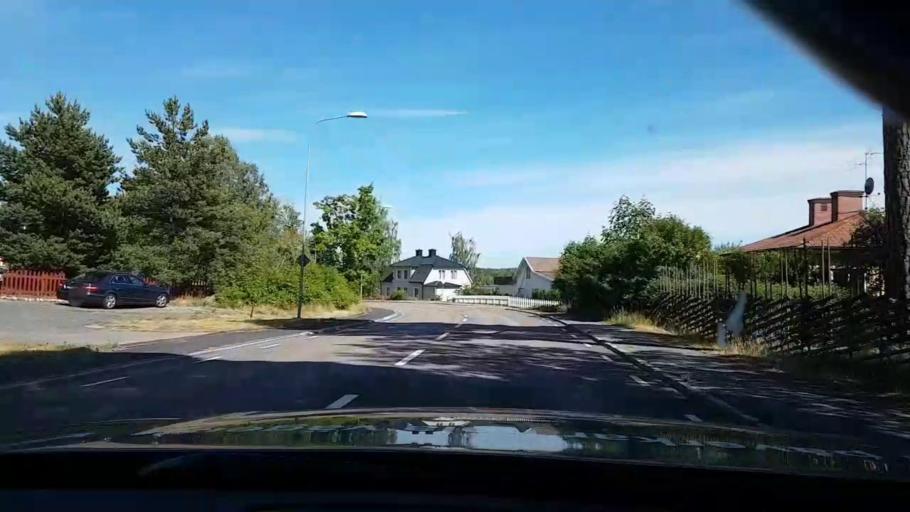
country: SE
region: Kalmar
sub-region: Vasterviks Kommun
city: Vaestervik
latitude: 57.9013
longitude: 16.6857
